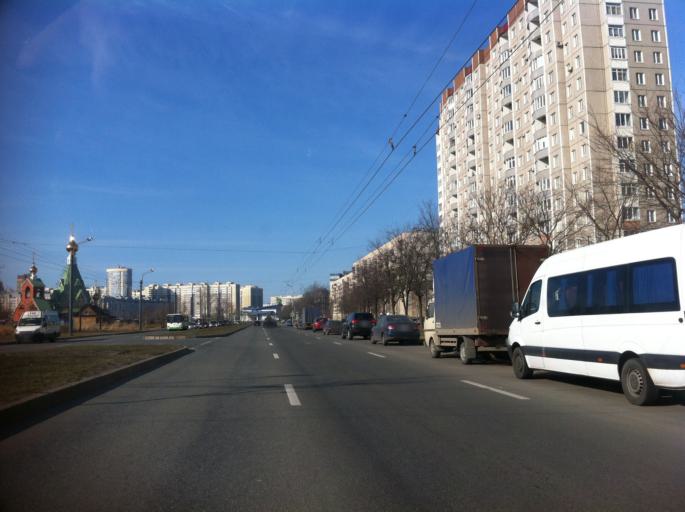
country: RU
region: St.-Petersburg
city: Uritsk
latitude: 59.8517
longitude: 30.1759
